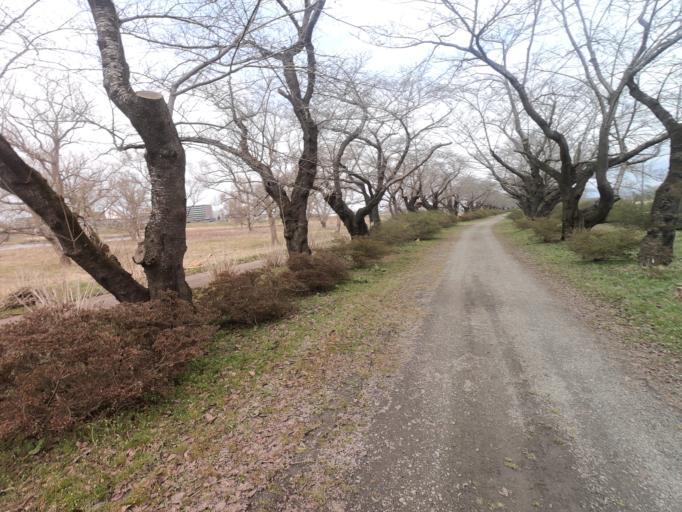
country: JP
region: Iwate
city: Kitakami
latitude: 39.2771
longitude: 141.1271
